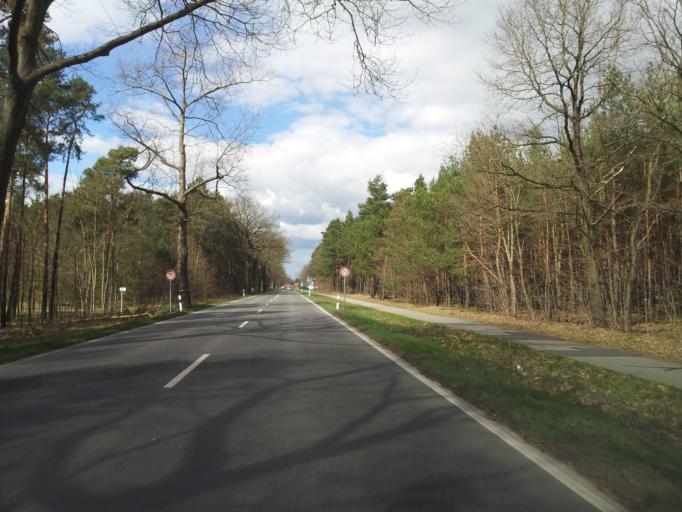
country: DE
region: Saxony
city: Wittichenau
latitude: 51.4167
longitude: 14.2835
